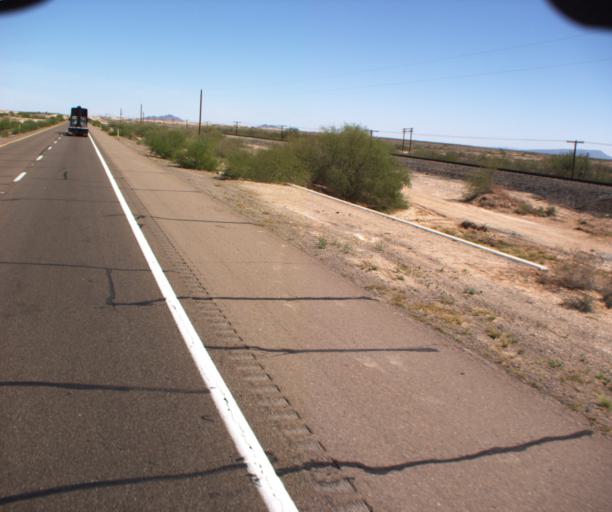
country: US
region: Arizona
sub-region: Yuma County
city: Wellton
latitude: 32.7527
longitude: -113.6557
